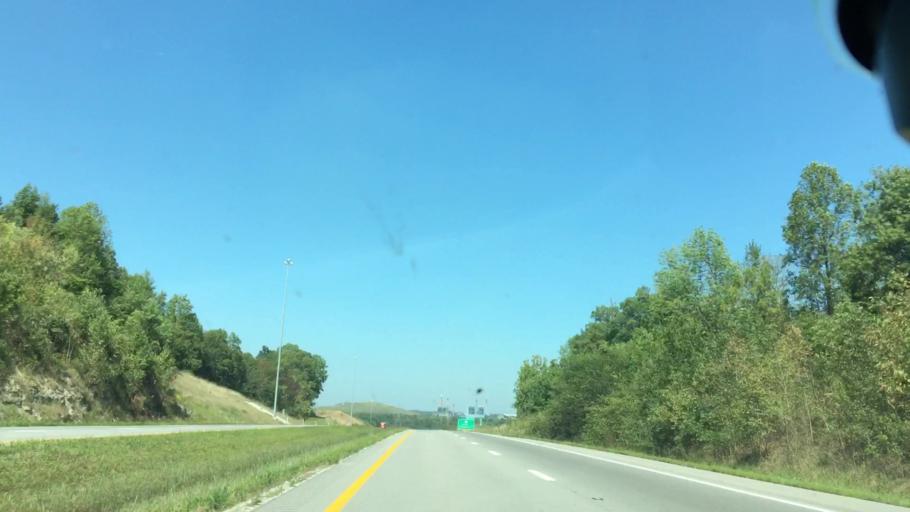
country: US
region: Kentucky
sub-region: Webster County
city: Sebree
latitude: 37.6019
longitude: -87.4964
